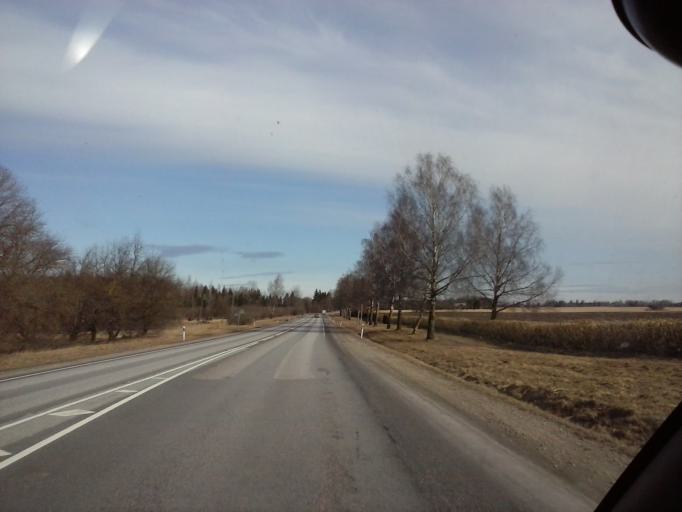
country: EE
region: Jaervamaa
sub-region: Paide linn
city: Paide
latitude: 58.9857
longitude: 25.5916
